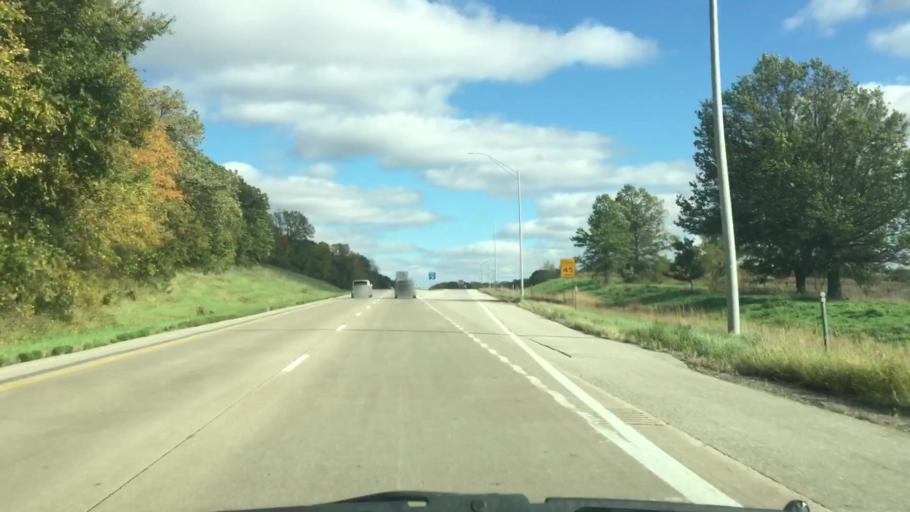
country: US
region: Iowa
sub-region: Muscatine County
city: Wilton
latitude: 41.6410
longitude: -91.0594
